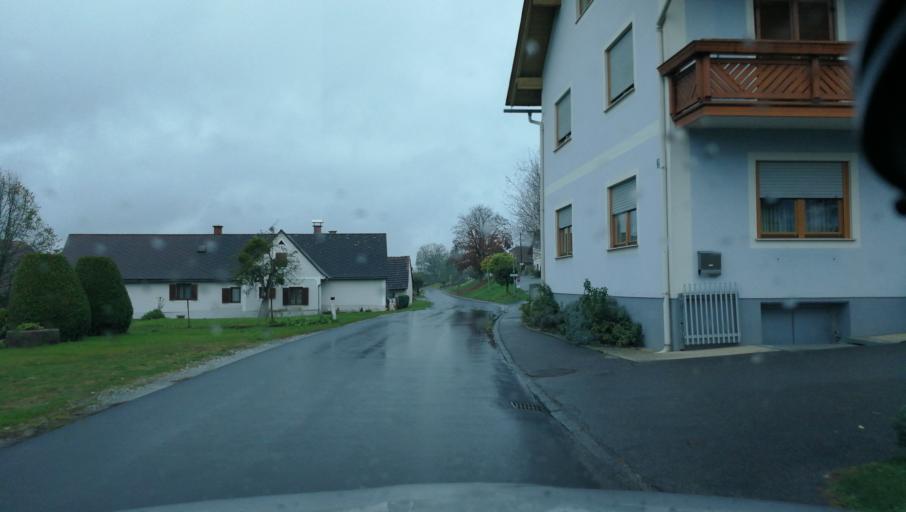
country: AT
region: Styria
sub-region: Politischer Bezirk Leibnitz
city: Strass in Steiermark
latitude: 46.7407
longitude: 15.6406
